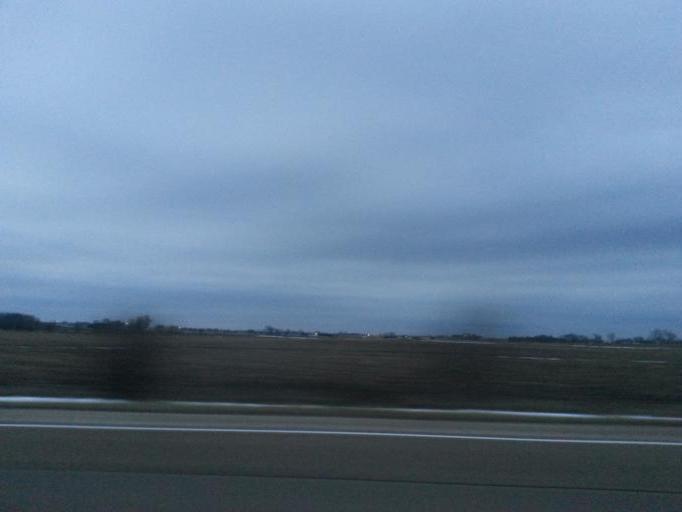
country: US
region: Iowa
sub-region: Black Hawk County
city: Elk Run Heights
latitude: 42.4166
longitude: -92.1763
